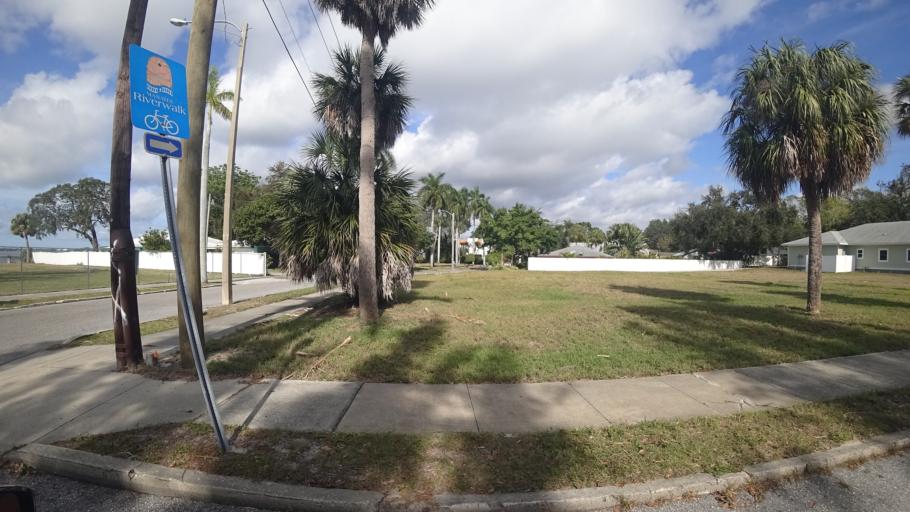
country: US
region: Florida
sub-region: Manatee County
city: Bradenton
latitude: 27.4990
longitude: -82.5796
